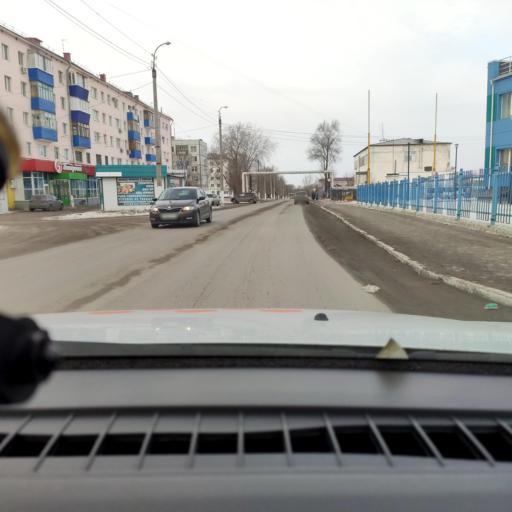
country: RU
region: Samara
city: Chapayevsk
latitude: 52.9578
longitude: 49.6913
